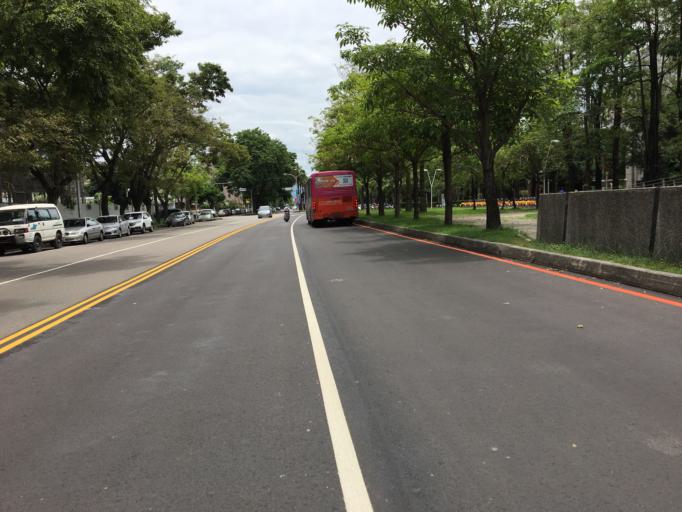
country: TW
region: Taiwan
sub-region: Taichung City
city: Taichung
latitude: 24.1241
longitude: 120.6765
